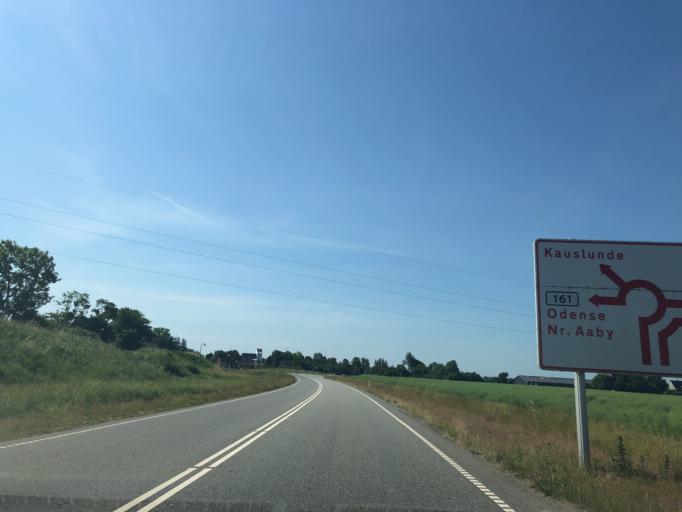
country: DK
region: South Denmark
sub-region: Middelfart Kommune
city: Strib
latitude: 55.4904
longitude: 9.8115
